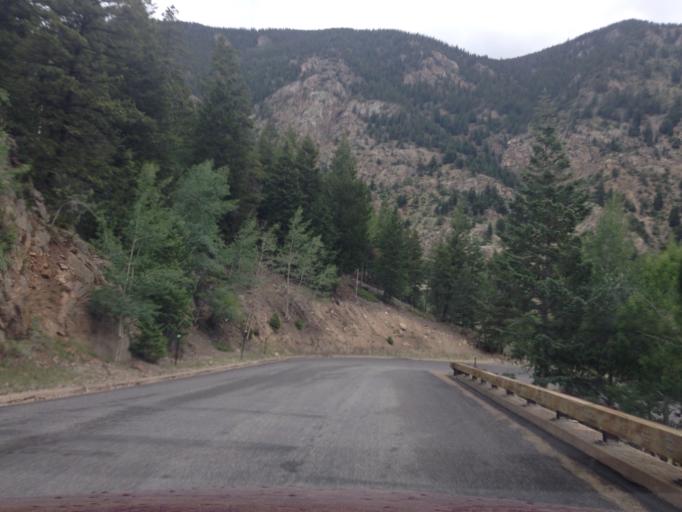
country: US
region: Colorado
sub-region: Clear Creek County
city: Georgetown
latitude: 39.7016
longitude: -105.7003
